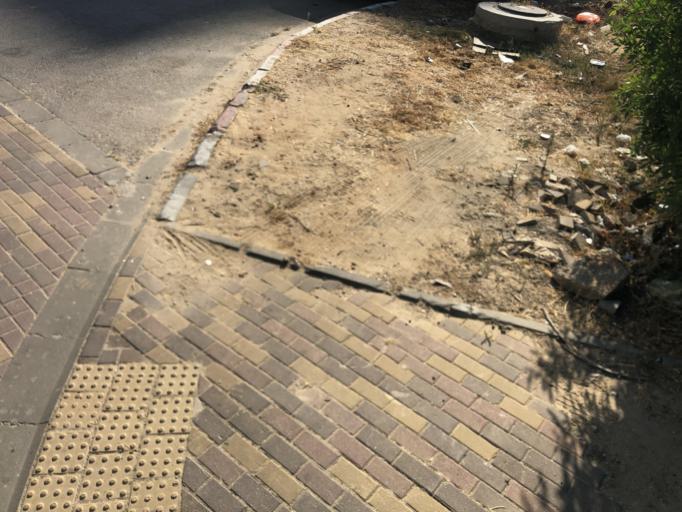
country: IL
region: Central District
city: Yehud
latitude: 32.0284
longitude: 34.8918
